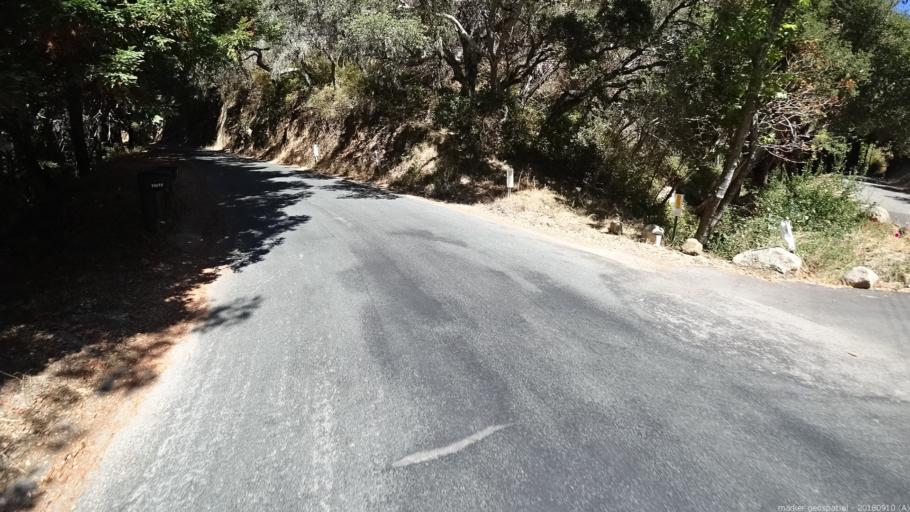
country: US
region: California
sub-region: Monterey County
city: Carmel Valley Village
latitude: 36.5058
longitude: -121.8081
